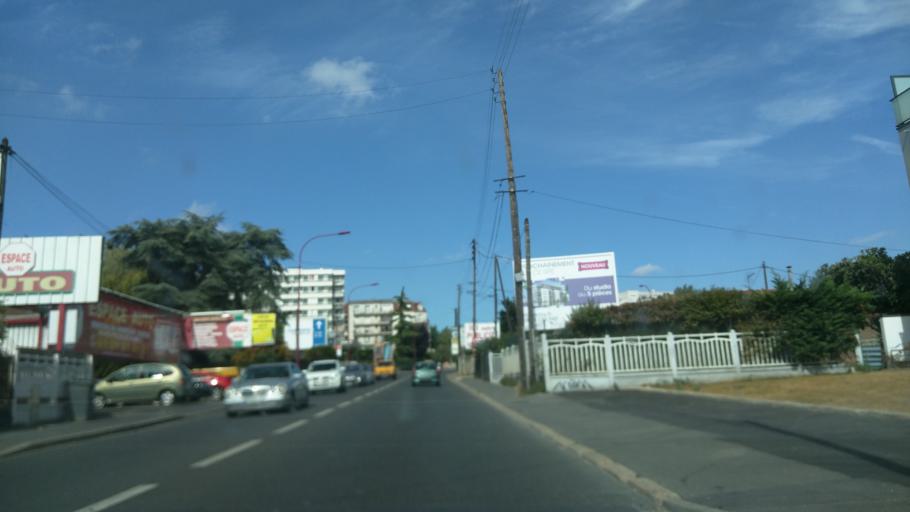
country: FR
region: Ile-de-France
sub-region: Departement du Val-d'Oise
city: Bezons
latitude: 48.9347
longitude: 2.2087
